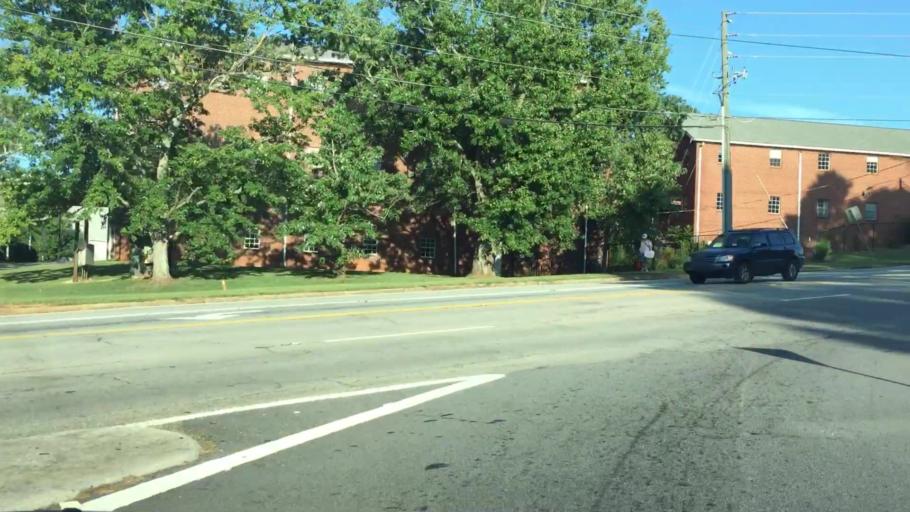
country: US
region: Georgia
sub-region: Clayton County
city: Morrow
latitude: 33.5601
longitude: -84.3217
